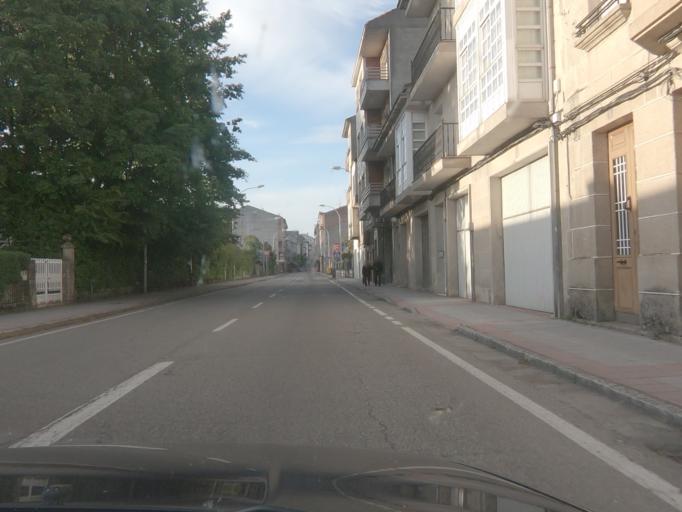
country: ES
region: Galicia
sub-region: Provincia de Ourense
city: Verin
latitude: 41.9346
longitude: -7.4388
